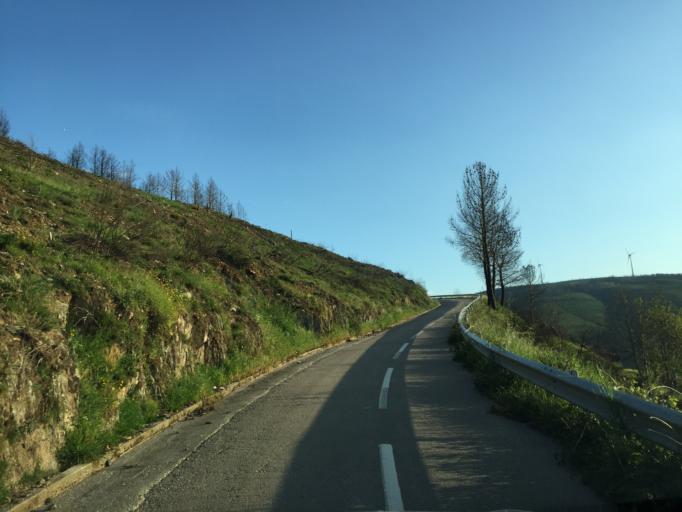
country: PT
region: Coimbra
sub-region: Arganil
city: Arganil
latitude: 40.1290
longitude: -8.0173
